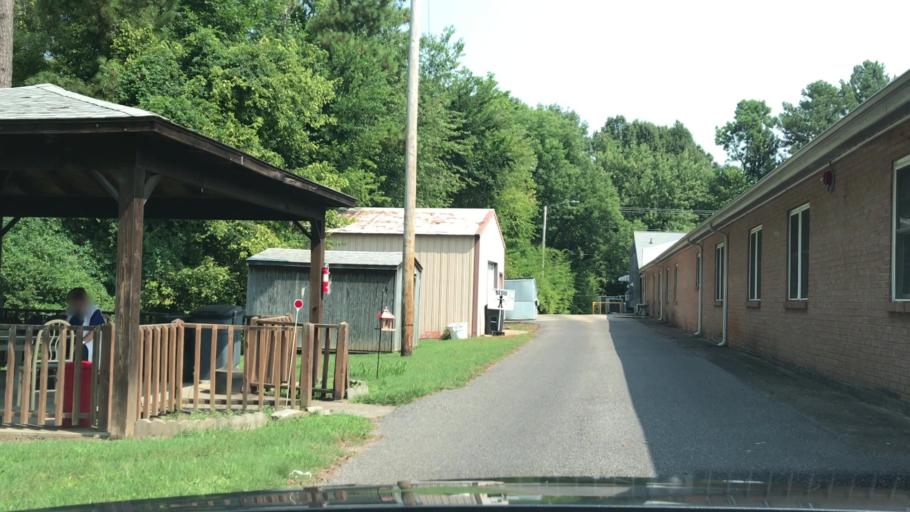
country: US
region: Kentucky
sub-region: Graves County
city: Mayfield
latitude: 36.7290
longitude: -88.6422
